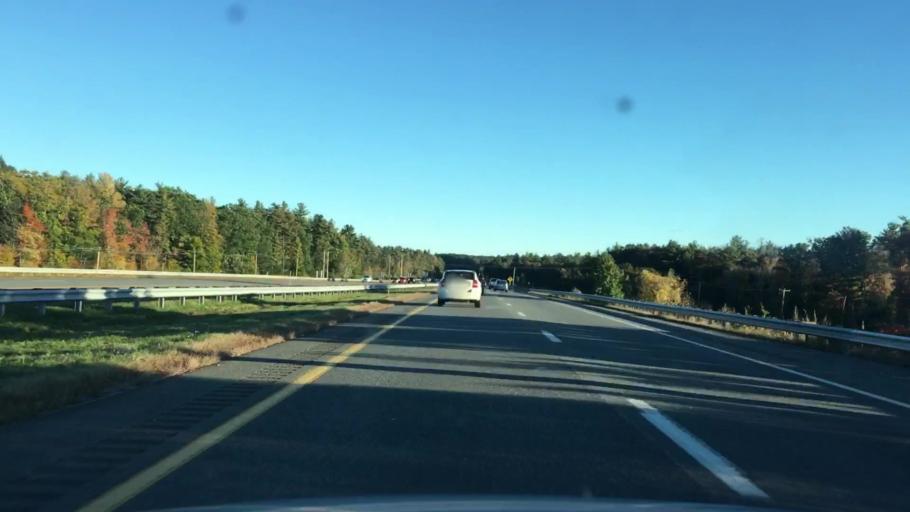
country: US
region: New Hampshire
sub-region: Rockingham County
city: Exeter
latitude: 42.9918
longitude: -70.9262
